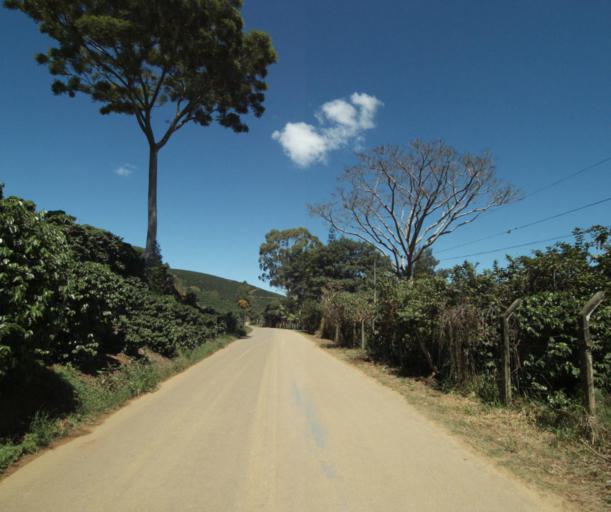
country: BR
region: Minas Gerais
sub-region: Espera Feliz
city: Espera Feliz
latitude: -20.5594
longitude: -41.8221
